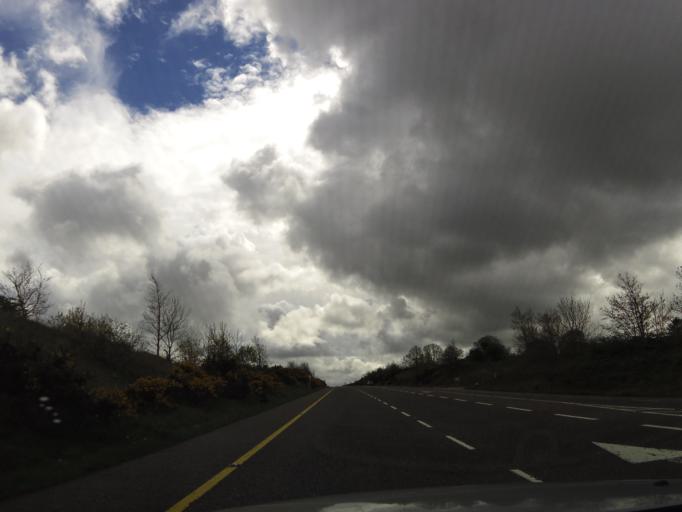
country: IE
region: Connaught
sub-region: Maigh Eo
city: Claremorris
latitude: 53.7673
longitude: -8.9582
